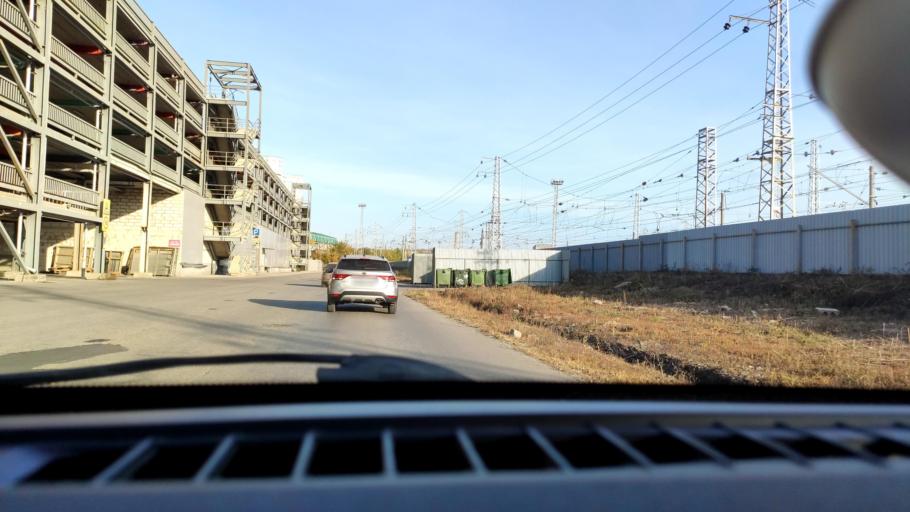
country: RU
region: Samara
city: Samara
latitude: 53.1857
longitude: 50.1278
